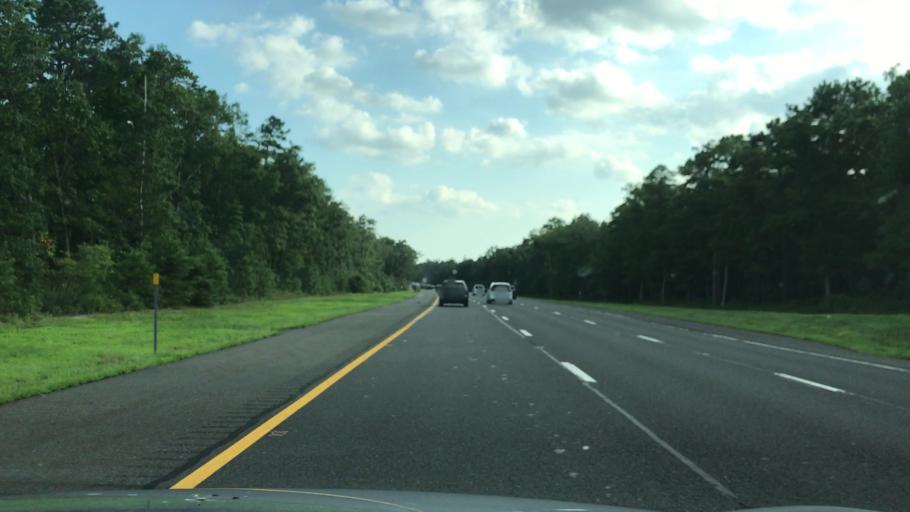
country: US
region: New Jersey
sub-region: Ocean County
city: Manahawkin
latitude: 39.6952
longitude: -74.2963
